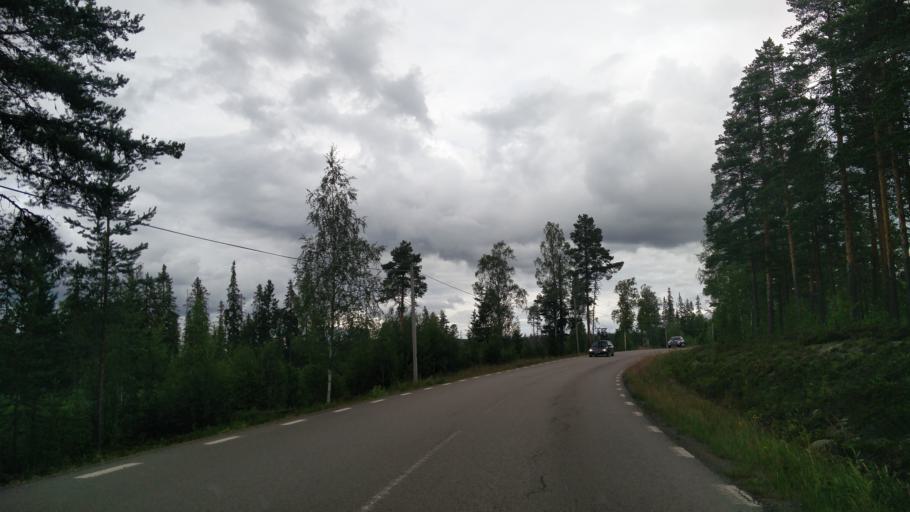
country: NO
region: Hedmark
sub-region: Trysil
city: Innbygda
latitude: 61.1627
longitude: 12.8224
